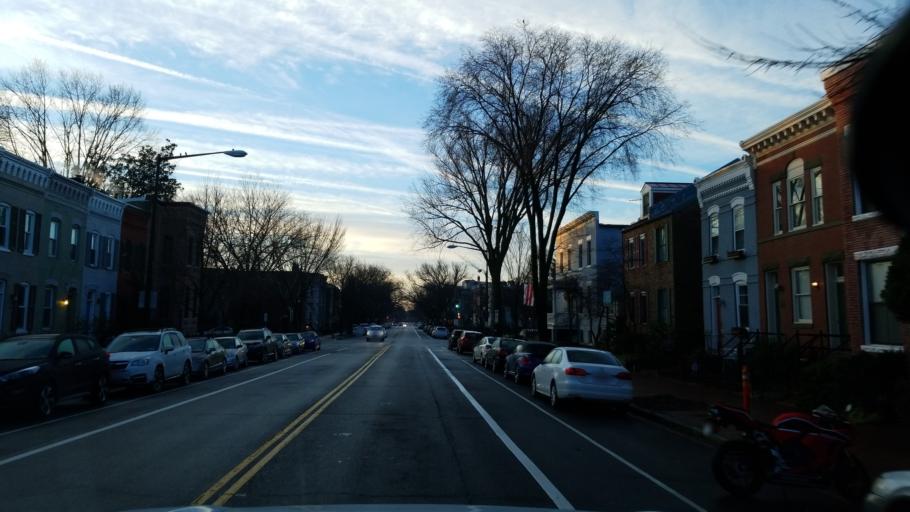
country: US
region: Washington, D.C.
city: Washington, D.C.
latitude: 38.8859
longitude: -76.9916
